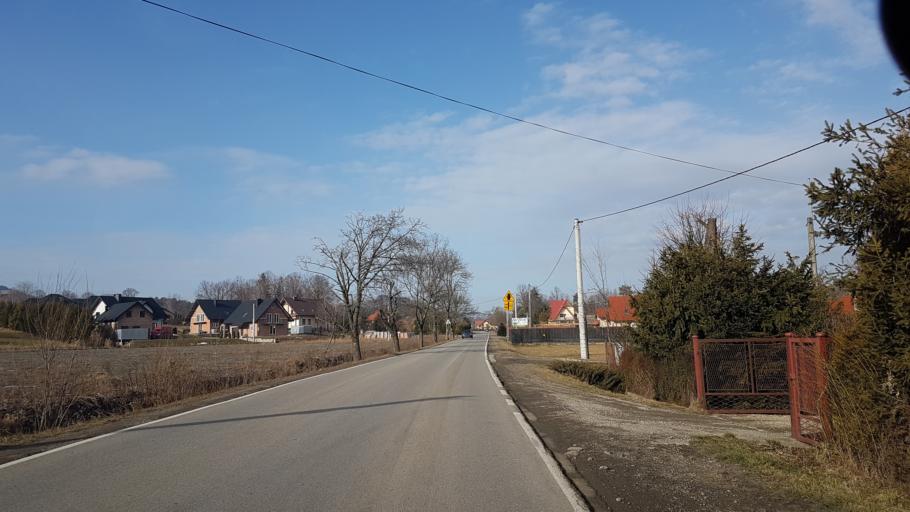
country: PL
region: Lesser Poland Voivodeship
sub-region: Powiat limanowski
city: Lukowica
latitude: 49.6530
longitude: 20.4967
